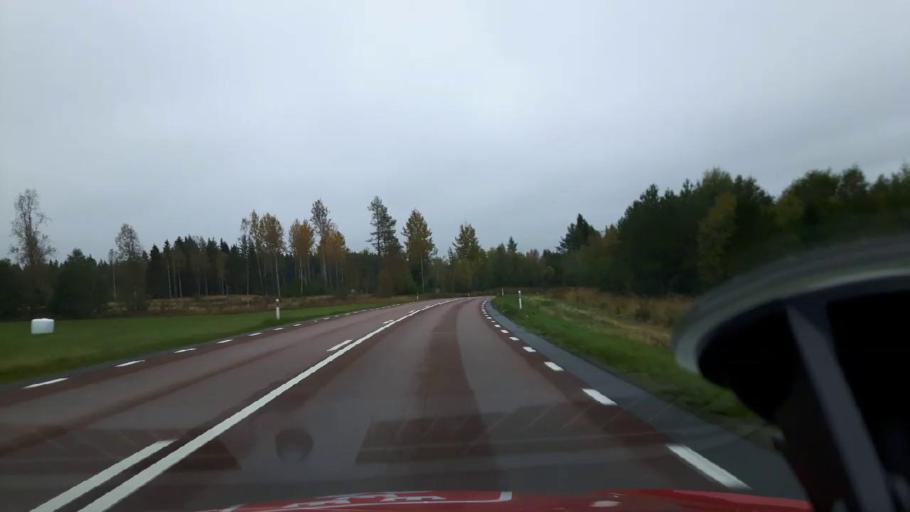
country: SE
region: Jaemtland
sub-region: Bergs Kommun
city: Hoverberg
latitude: 62.7588
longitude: 14.4377
